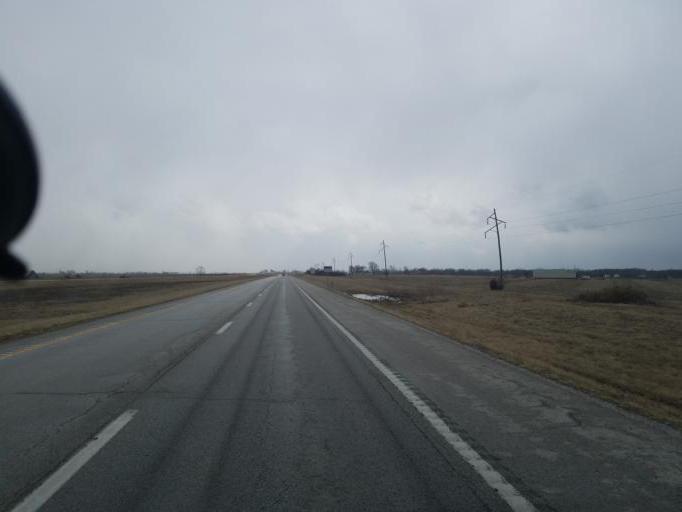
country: US
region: Missouri
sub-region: Randolph County
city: Moberly
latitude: 39.5411
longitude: -92.4500
